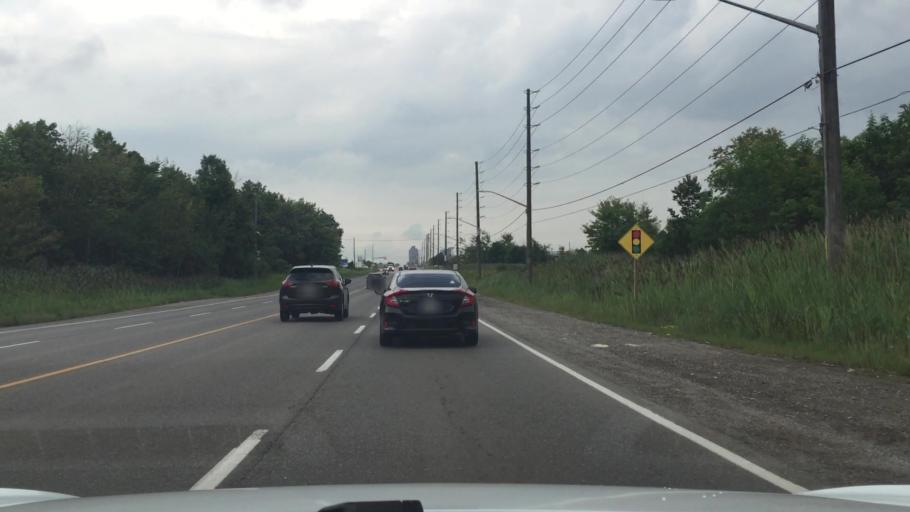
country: CA
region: Ontario
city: Ajax
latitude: 43.8371
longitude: -79.0575
